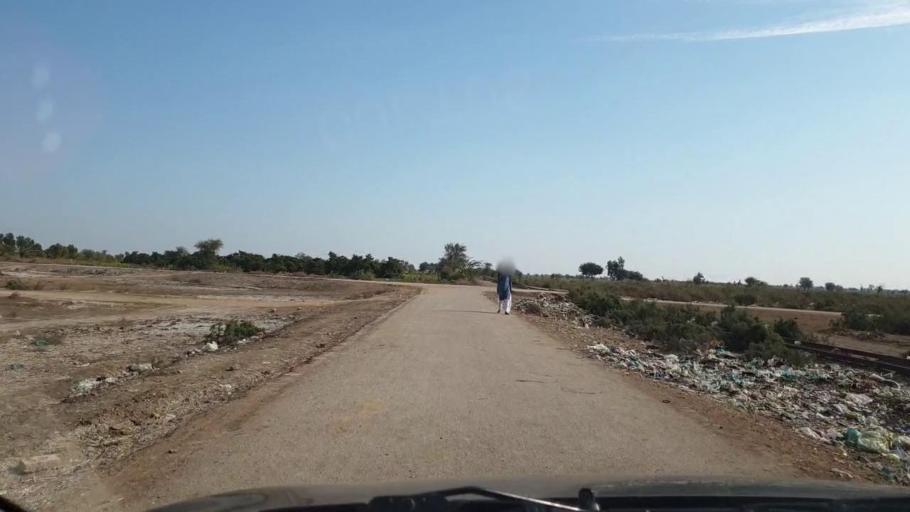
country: PK
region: Sindh
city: Sinjhoro
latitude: 26.0298
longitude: 68.8147
